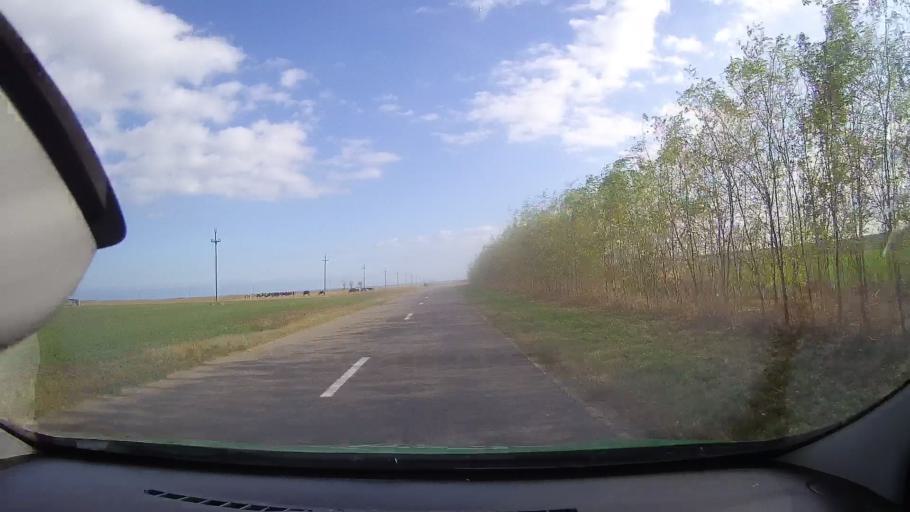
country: RO
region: Constanta
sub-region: Comuna Istria
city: Nuntasi
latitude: 44.5334
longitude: 28.6676
